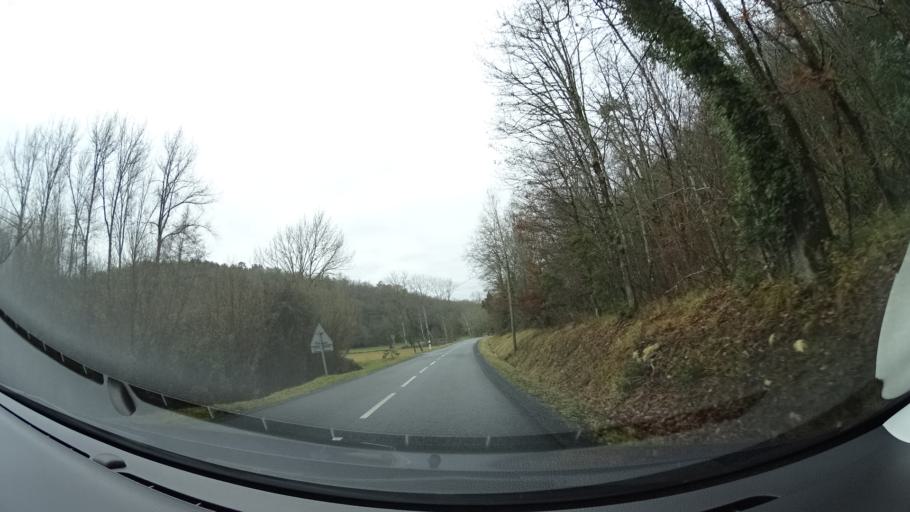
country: FR
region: Aquitaine
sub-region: Departement de la Dordogne
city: Saint-Cyprien
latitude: 44.8856
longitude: 1.0931
